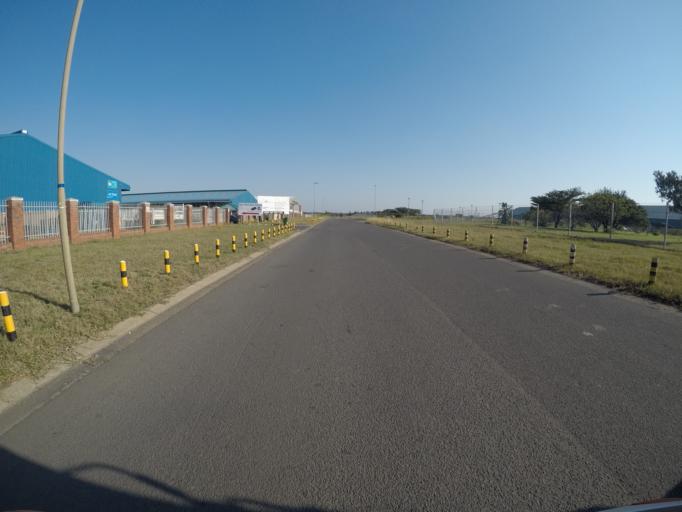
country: ZA
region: KwaZulu-Natal
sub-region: uThungulu District Municipality
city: Richards Bay
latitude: -28.7470
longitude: 32.0243
